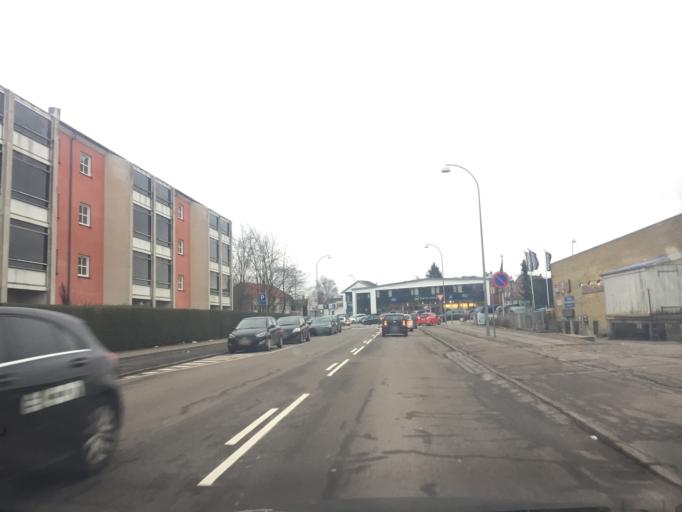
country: DK
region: Zealand
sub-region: Roskilde Kommune
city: Roskilde
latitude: 55.6348
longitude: 12.0705
